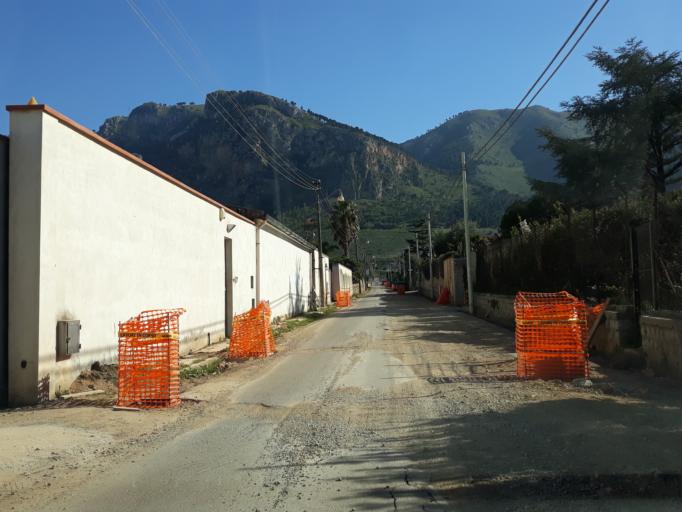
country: IT
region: Sicily
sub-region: Palermo
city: Villa Ciambra
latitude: 38.0826
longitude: 13.3460
